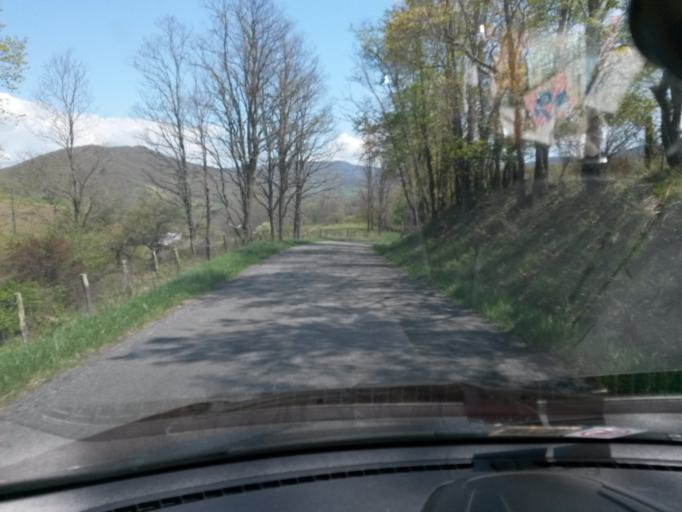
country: US
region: Virginia
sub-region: Highland County
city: Monterey
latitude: 38.2914
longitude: -79.6196
